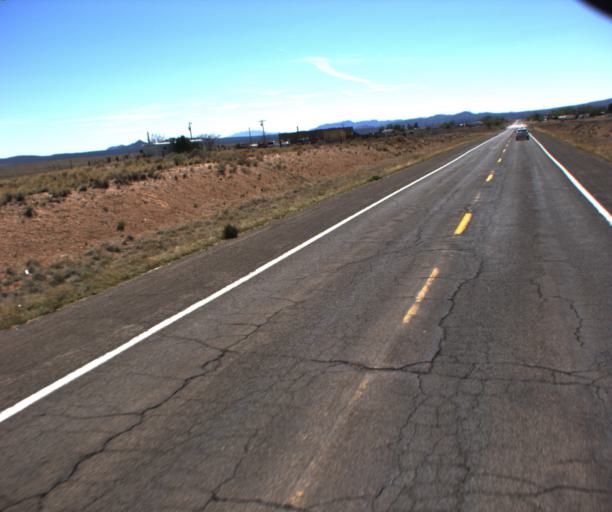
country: US
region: Arizona
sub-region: Mohave County
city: Peach Springs
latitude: 35.4884
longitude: -113.5561
